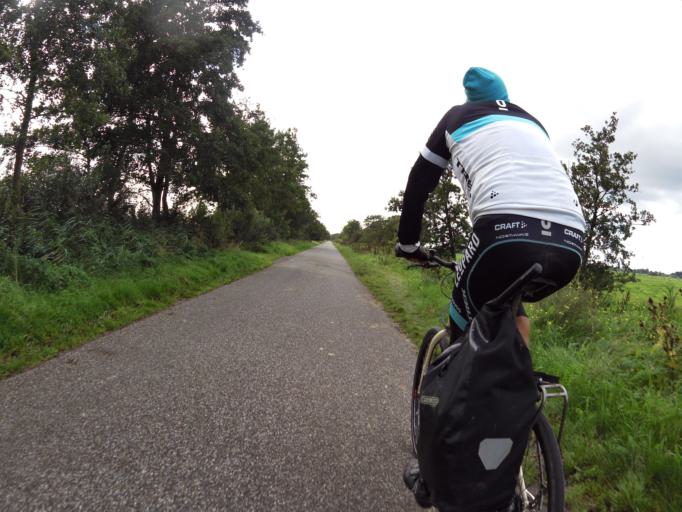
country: NL
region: North Holland
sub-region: Gemeente Wijdemeren
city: Nieuw-Loosdrecht
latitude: 52.1800
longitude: 5.1401
